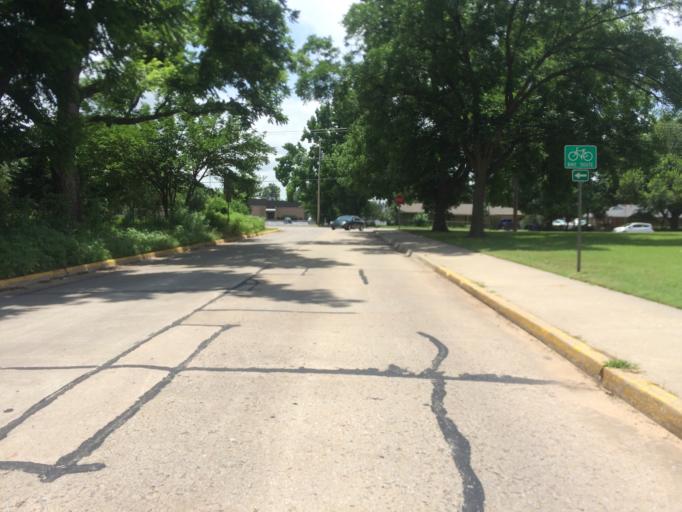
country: US
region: Oklahoma
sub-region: Cleveland County
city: Norman
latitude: 35.2118
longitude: -97.4690
